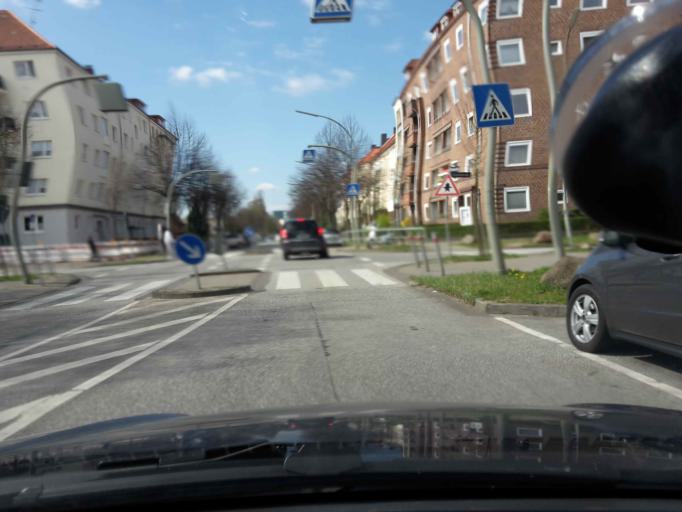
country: DE
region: Hamburg
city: Rothenburgsort
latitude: 53.5496
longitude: 10.0563
